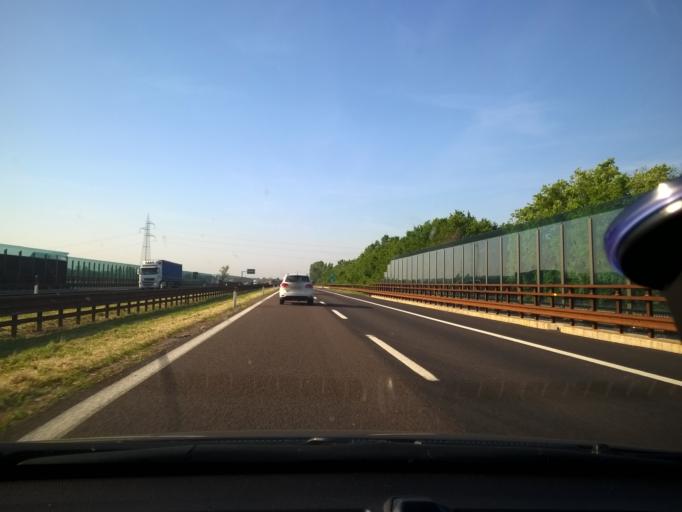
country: IT
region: Emilia-Romagna
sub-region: Provincia di Modena
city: Santa Croce Scuole
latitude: 44.7520
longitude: 10.8442
